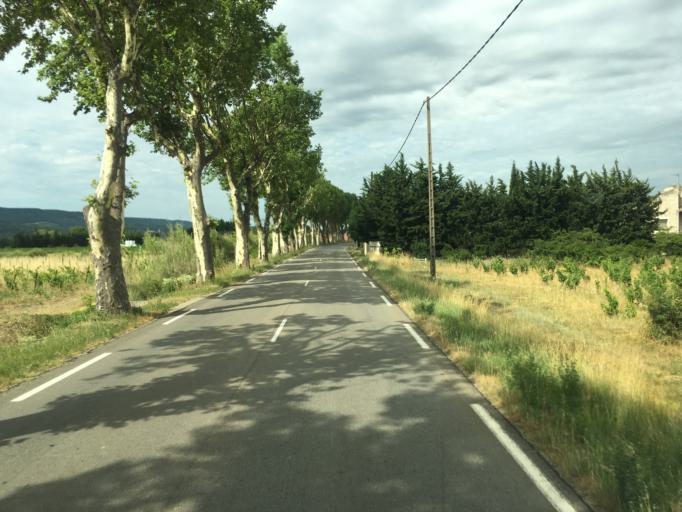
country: FR
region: Rhone-Alpes
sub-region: Departement de la Drome
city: Vinsobres
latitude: 44.3009
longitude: 5.0188
